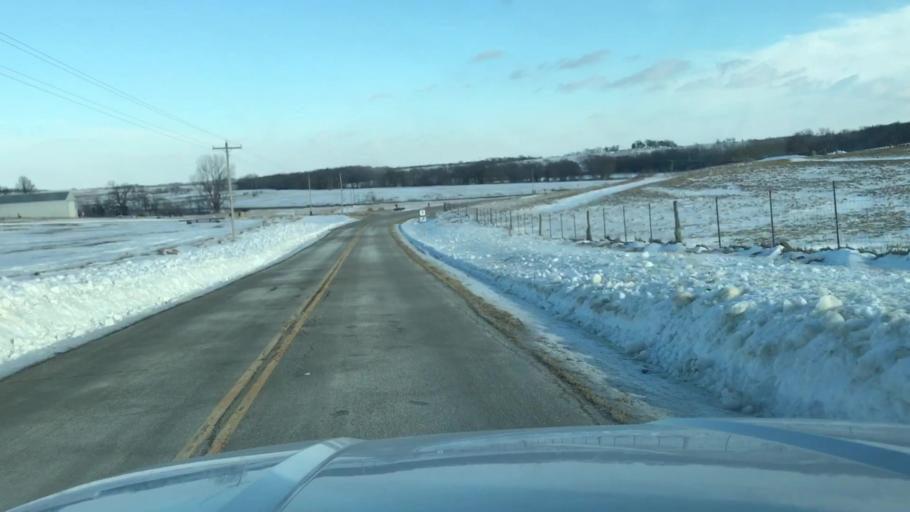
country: US
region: Missouri
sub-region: Holt County
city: Oregon
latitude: 40.1006
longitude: -94.9790
